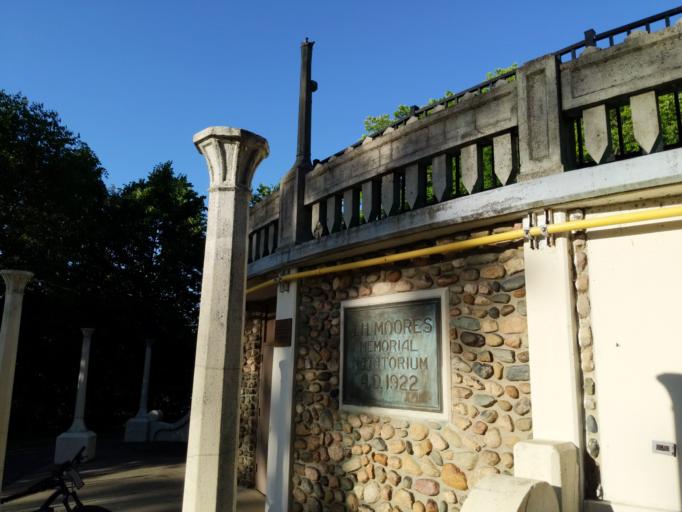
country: US
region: Michigan
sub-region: Ingham County
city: Lansing
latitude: 42.7169
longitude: -84.5568
